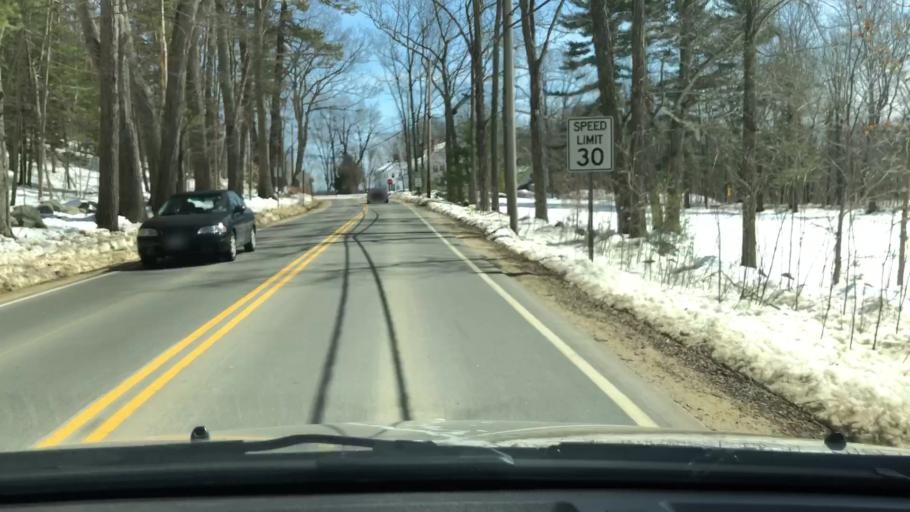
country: US
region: New Hampshire
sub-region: Strafford County
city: Madbury
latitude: 43.1664
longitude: -70.9388
